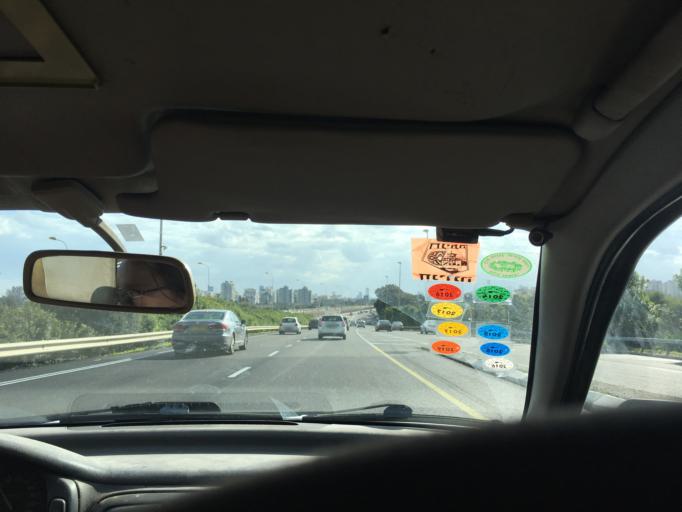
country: IL
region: Tel Aviv
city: Ramat HaSharon
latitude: 32.1383
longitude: 34.8091
